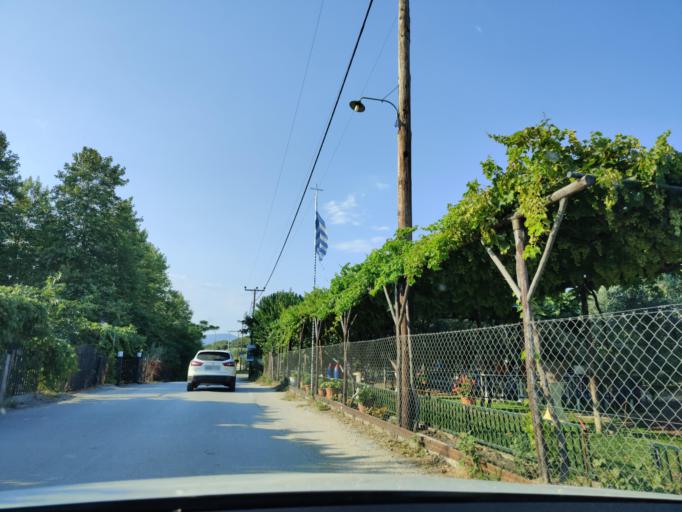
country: GR
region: East Macedonia and Thrace
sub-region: Nomos Kavalas
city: Nea Peramos
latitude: 40.8214
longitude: 24.3079
